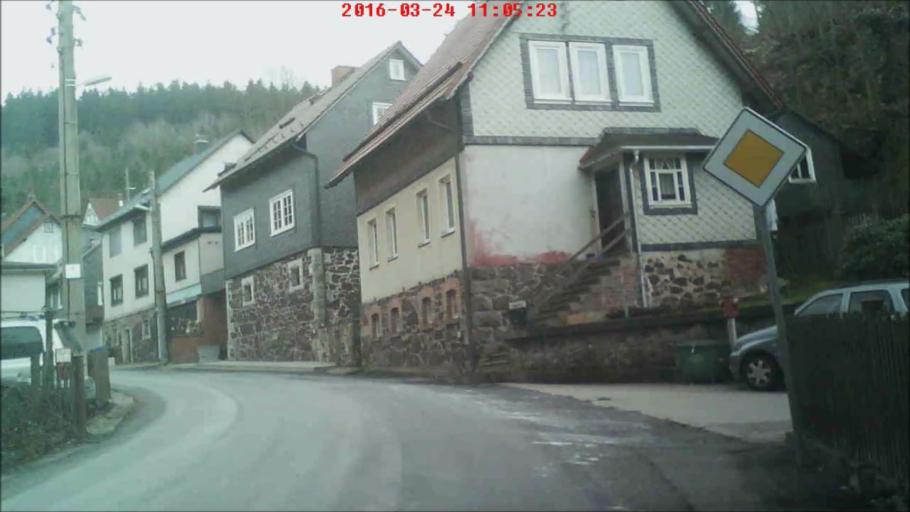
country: DE
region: Thuringia
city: Neustadt am Rennsteig
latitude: 50.5367
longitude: 10.9200
